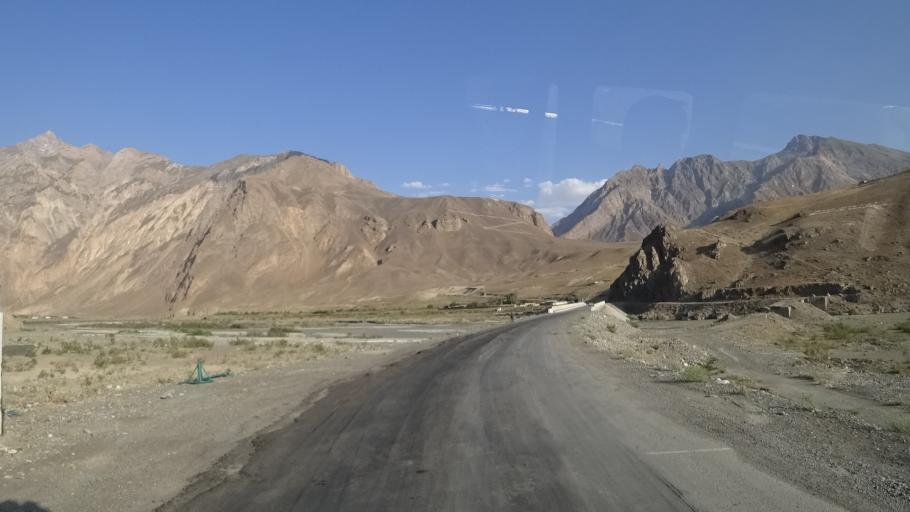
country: TJ
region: Gorno-Badakhshan
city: Vanj
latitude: 38.2996
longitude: 71.3370
